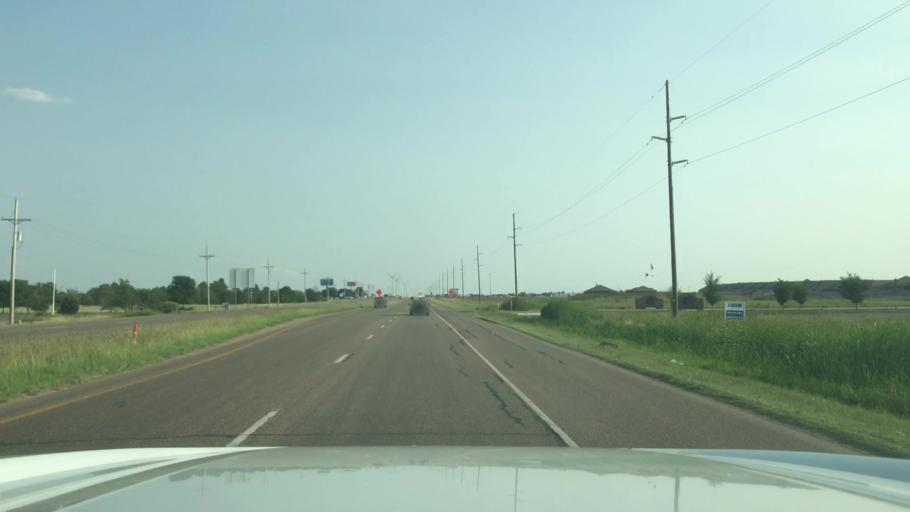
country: US
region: Texas
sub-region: Potter County
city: Amarillo
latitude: 35.1312
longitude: -101.9382
